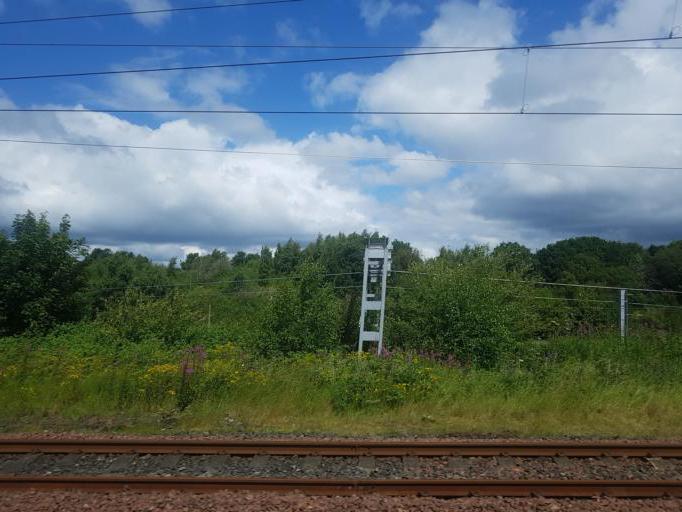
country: GB
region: Scotland
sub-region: Falkirk
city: Polmont
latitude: 55.9857
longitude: -3.7281
